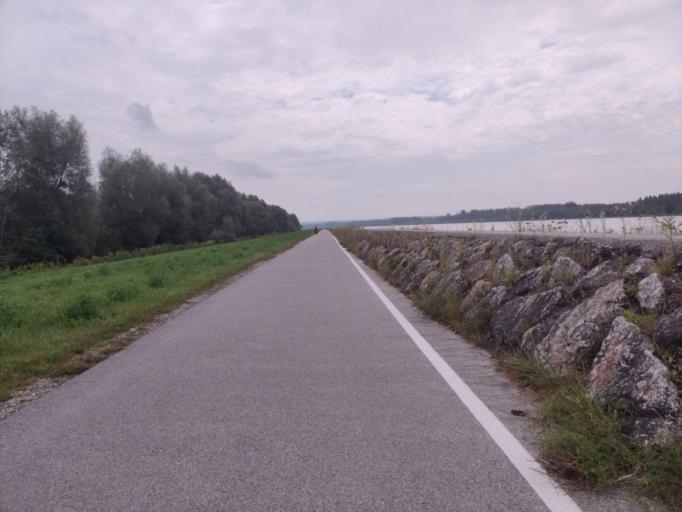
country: AT
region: Upper Austria
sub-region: Politischer Bezirk Perg
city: Perg
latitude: 48.2181
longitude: 14.5933
